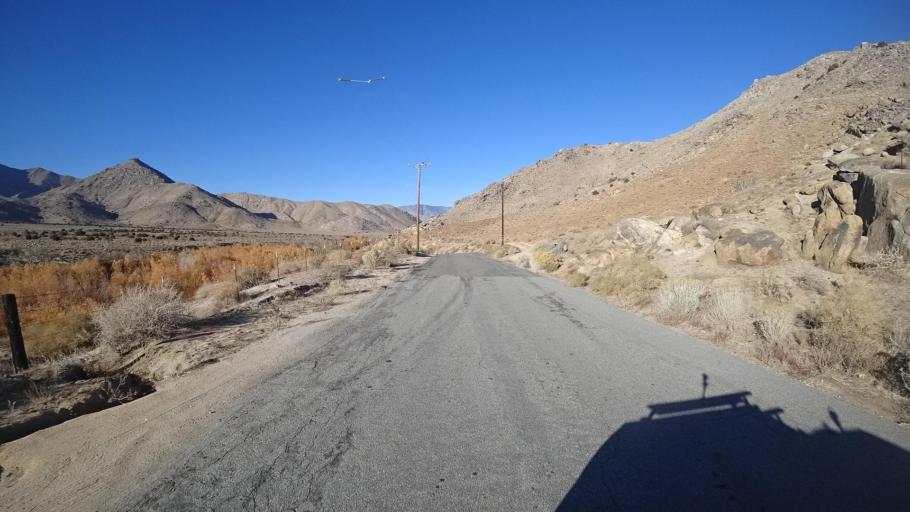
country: US
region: California
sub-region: Kern County
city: Weldon
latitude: 35.5717
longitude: -118.2505
